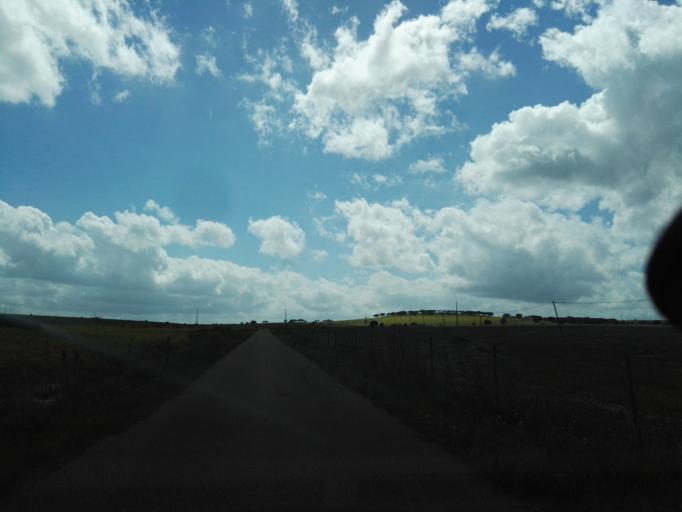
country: PT
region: Portalegre
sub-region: Elvas
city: Elvas
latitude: 38.9643
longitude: -7.1745
